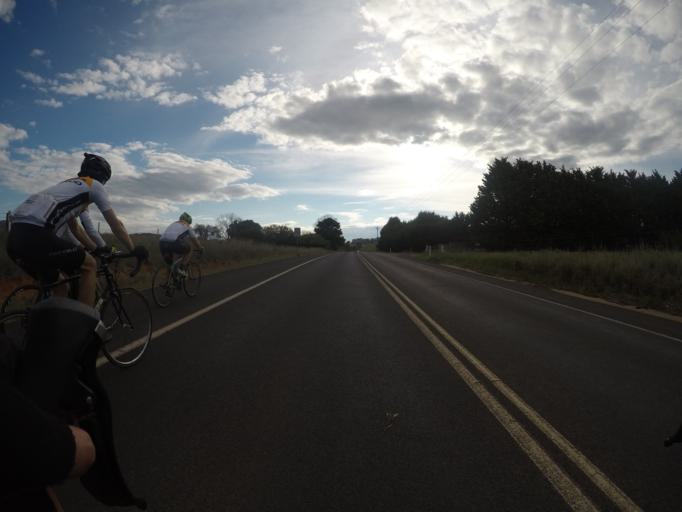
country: AU
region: New South Wales
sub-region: Orange Municipality
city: Orange
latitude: -33.2954
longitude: 149.0057
